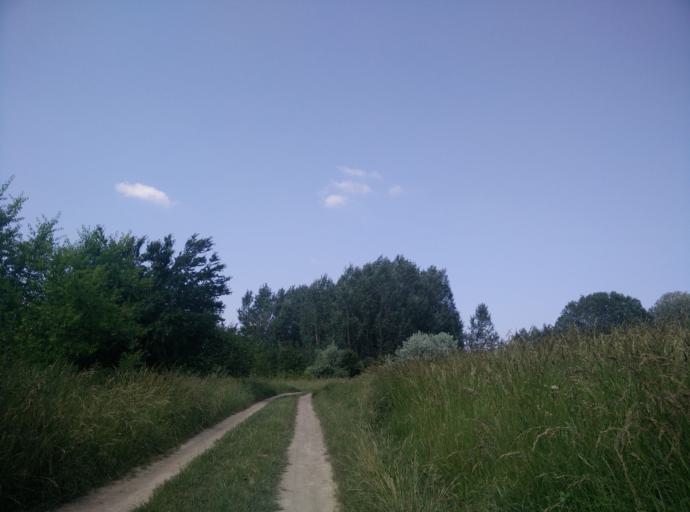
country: HU
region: Pest
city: Biatorbagy
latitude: 47.4760
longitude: 18.8060
